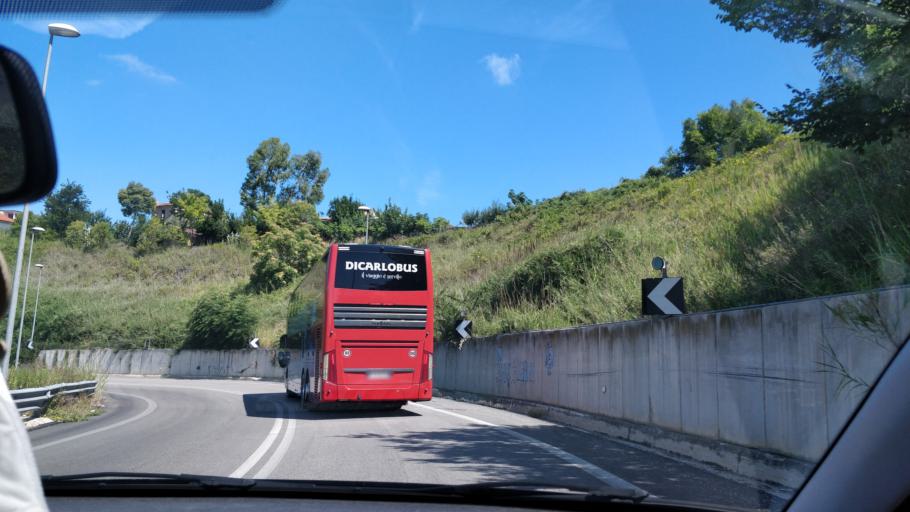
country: IT
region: Abruzzo
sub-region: Provincia di Chieti
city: Francavilla al Mare
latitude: 42.4055
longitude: 14.3036
